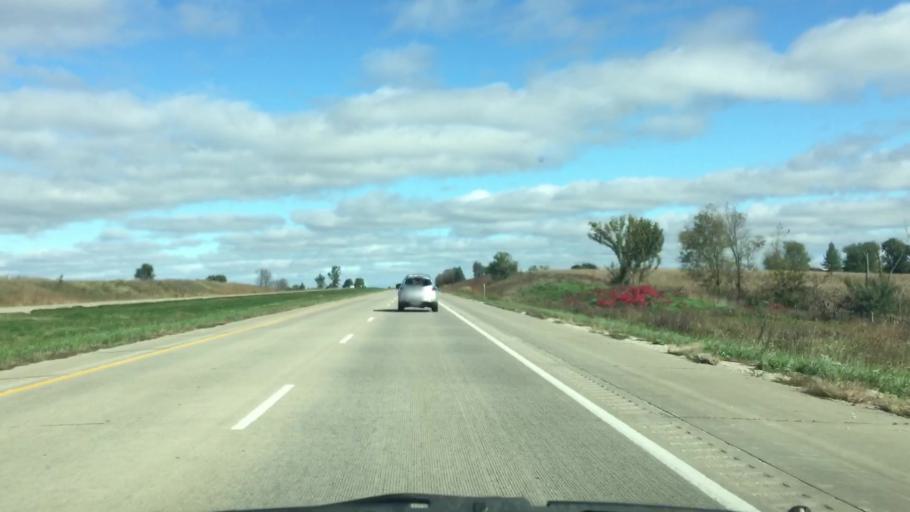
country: US
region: Iowa
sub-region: Decatur County
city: Leon
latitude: 40.7746
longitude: -93.8357
